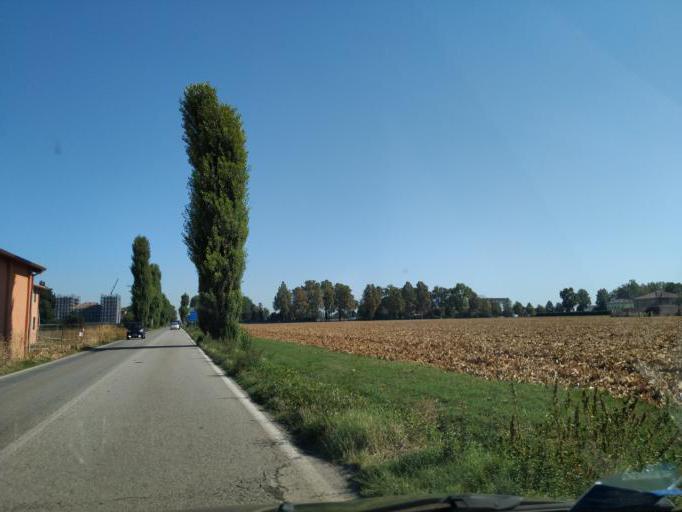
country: IT
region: Emilia-Romagna
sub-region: Provincia di Ferrara
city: Cento
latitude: 44.7318
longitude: 11.2621
